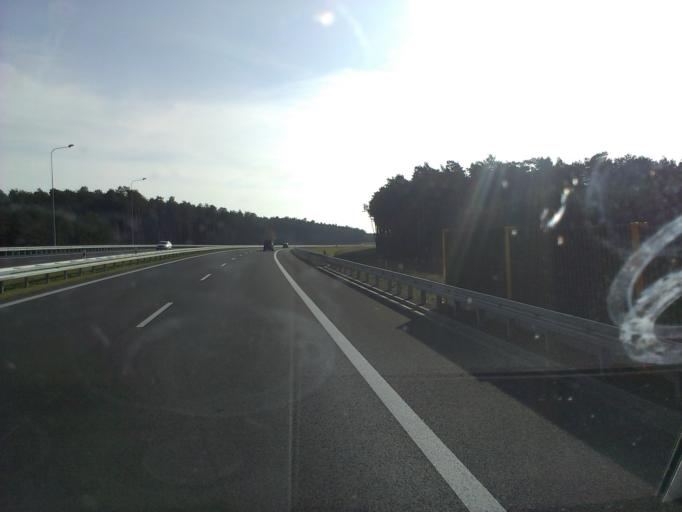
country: PL
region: Lubusz
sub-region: Powiat miedzyrzecki
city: Skwierzyna
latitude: 52.5548
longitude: 15.5366
